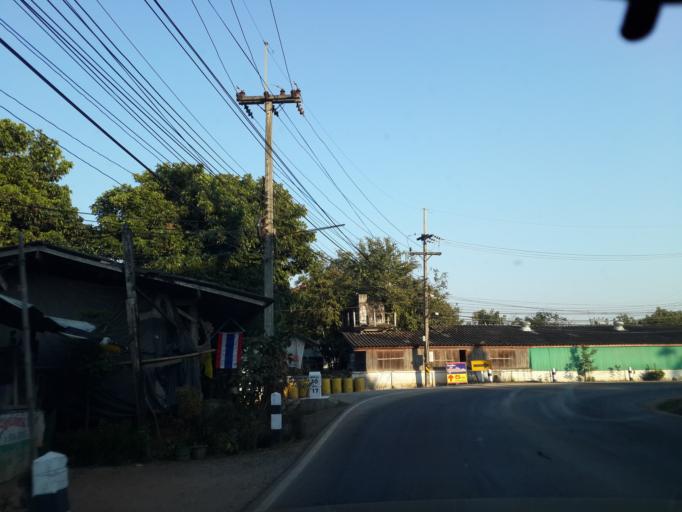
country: TH
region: Chiang Mai
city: Chai Prakan
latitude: 19.8026
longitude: 99.1501
